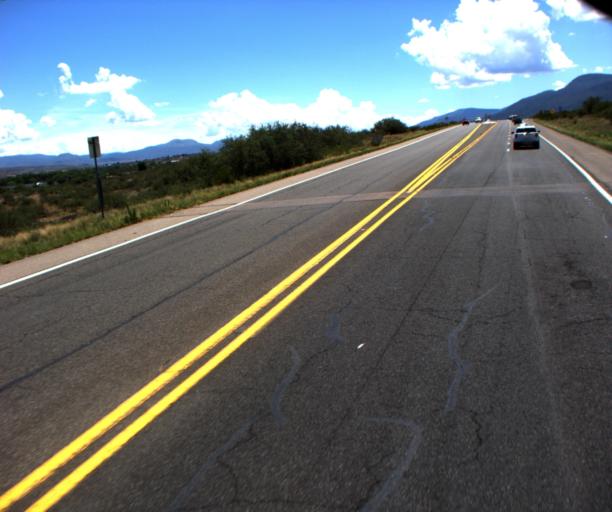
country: US
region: Arizona
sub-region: Yavapai County
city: Camp Verde
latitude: 34.5876
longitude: -111.8875
